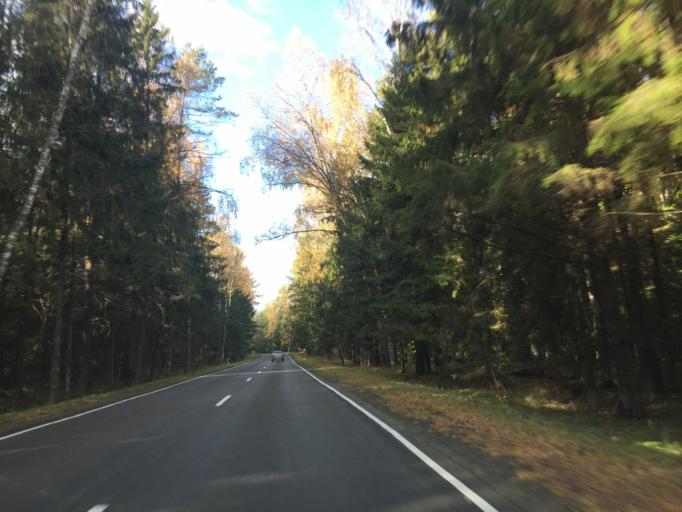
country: BY
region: Minsk
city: Svir
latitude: 54.9227
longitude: 26.5093
